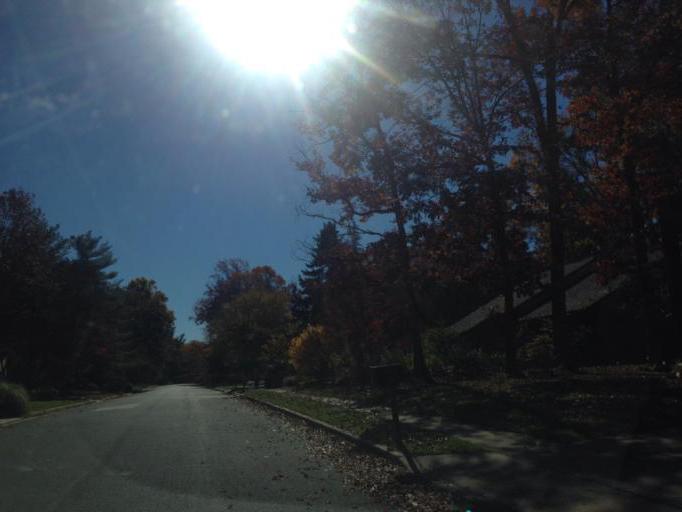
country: US
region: Maryland
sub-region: Howard County
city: Riverside
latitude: 39.2036
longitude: -76.8740
